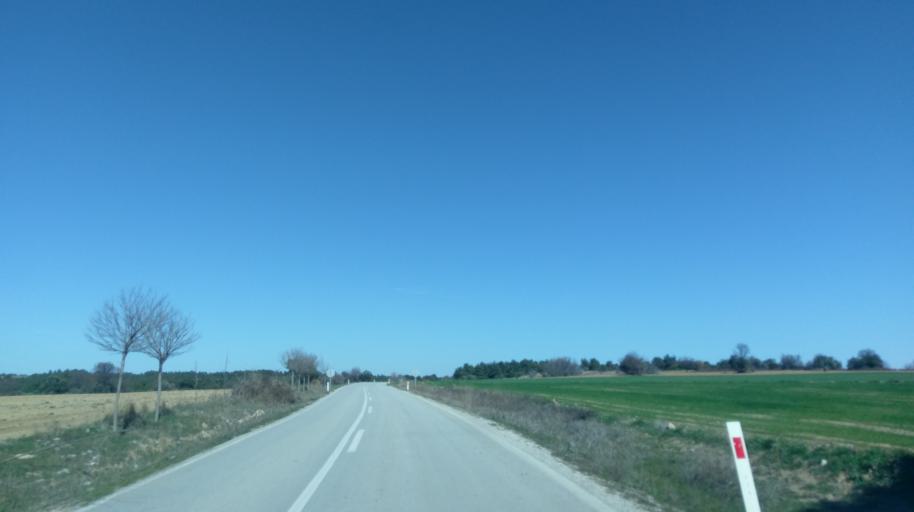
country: TR
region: Canakkale
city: Intepe
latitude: 40.0993
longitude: 26.2282
